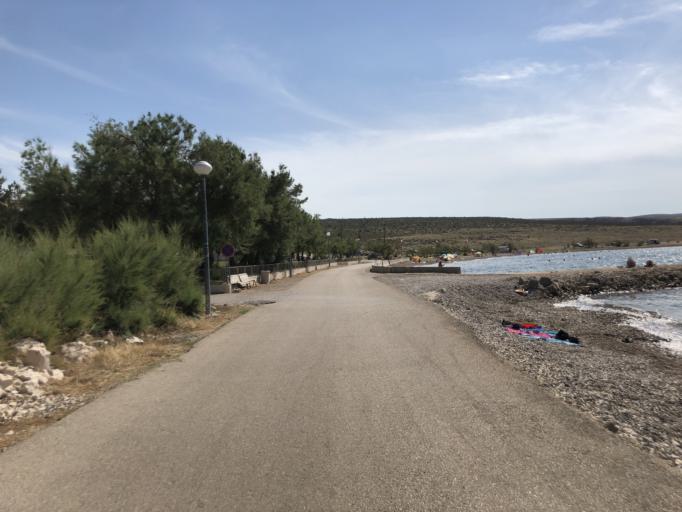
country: HR
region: Zadarska
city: Posedarje
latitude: 44.2467
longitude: 15.5364
